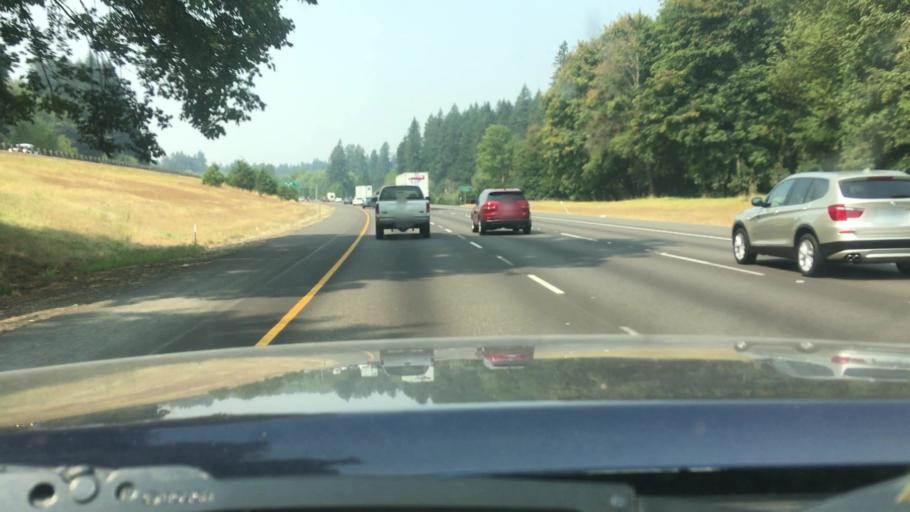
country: US
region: Oregon
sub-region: Clackamas County
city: Stafford
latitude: 45.3737
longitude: -122.7333
